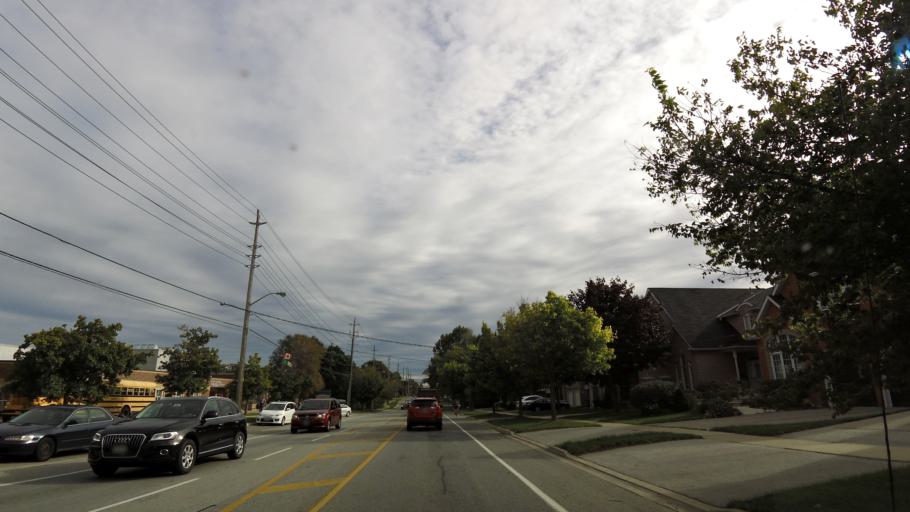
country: CA
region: Ontario
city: Etobicoke
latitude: 43.6366
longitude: -79.5069
